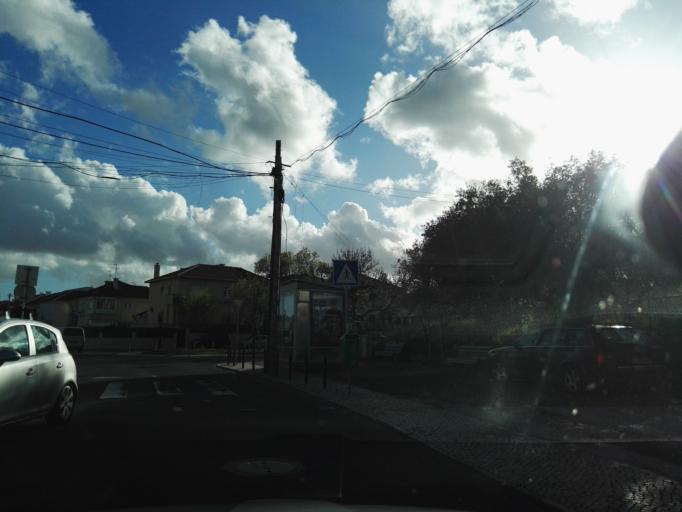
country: PT
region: Lisbon
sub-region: Loures
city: Moscavide
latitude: 38.7776
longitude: -9.1198
